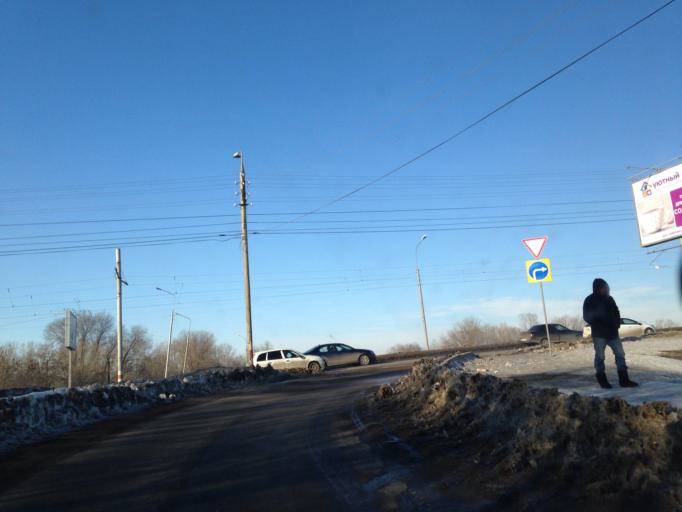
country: RU
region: Ulyanovsk
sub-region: Ulyanovskiy Rayon
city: Ulyanovsk
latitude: 54.2925
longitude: 48.3141
